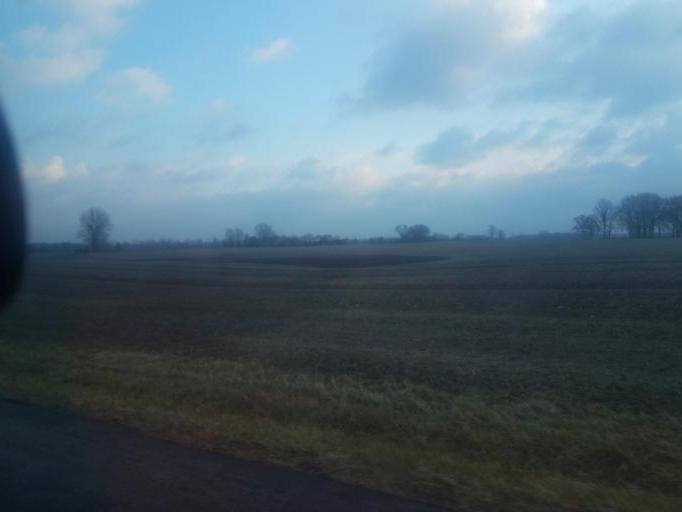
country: US
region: Ohio
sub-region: Marion County
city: Marion
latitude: 40.6346
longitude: -83.1885
